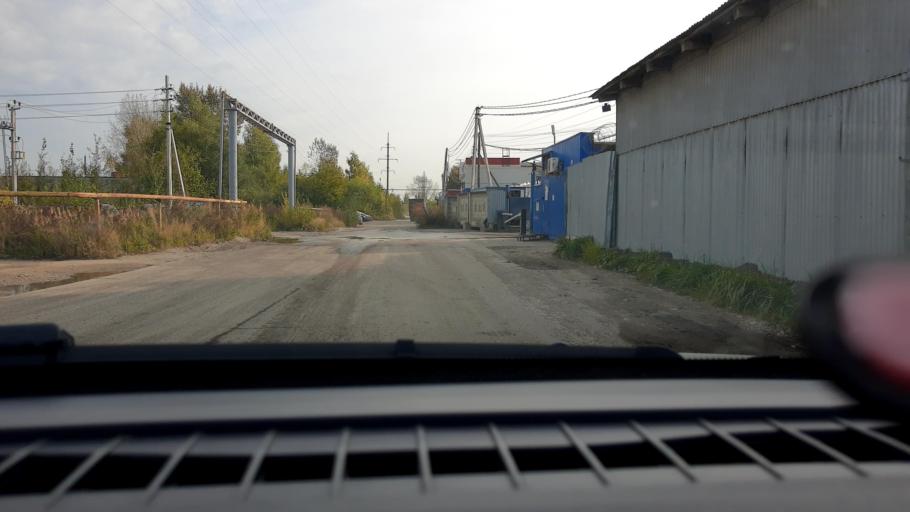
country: RU
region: Nizjnij Novgorod
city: Burevestnik
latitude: 56.1647
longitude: 43.9068
